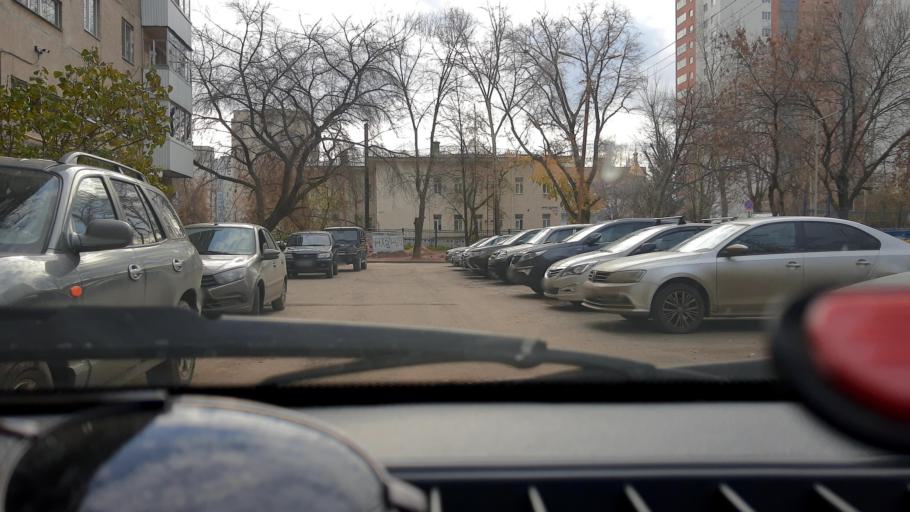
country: RU
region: Bashkortostan
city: Ufa
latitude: 54.7841
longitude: 56.1333
